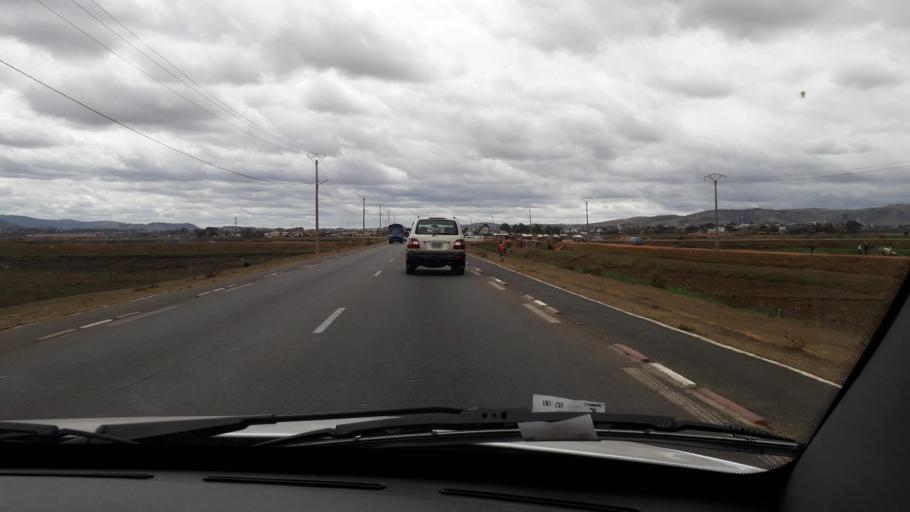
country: MG
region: Analamanga
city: Antananarivo
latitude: -18.8198
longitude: 47.5160
